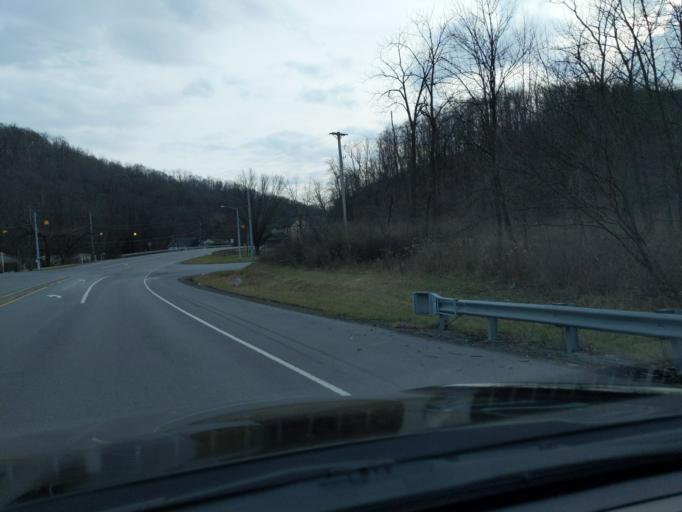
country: US
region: Pennsylvania
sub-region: Blair County
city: Lakemont
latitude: 40.4526
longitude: -78.3528
